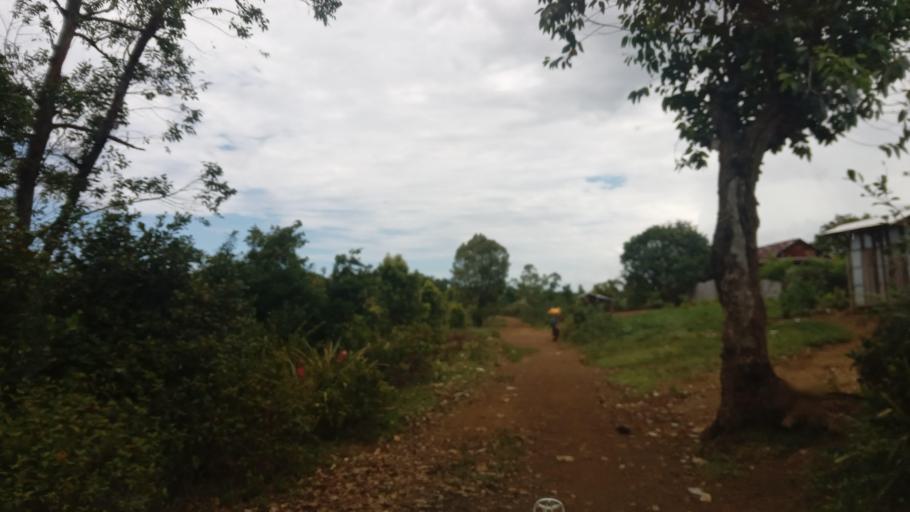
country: MG
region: Atsimo-Atsinanana
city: Vohipaho
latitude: -23.6203
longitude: 47.5795
